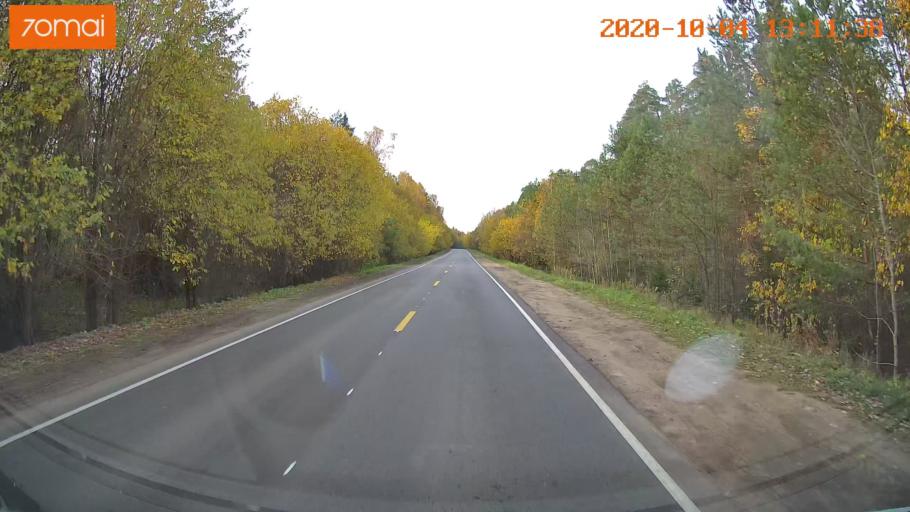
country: RU
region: Ivanovo
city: Bogorodskoye
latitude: 57.0782
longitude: 40.9413
